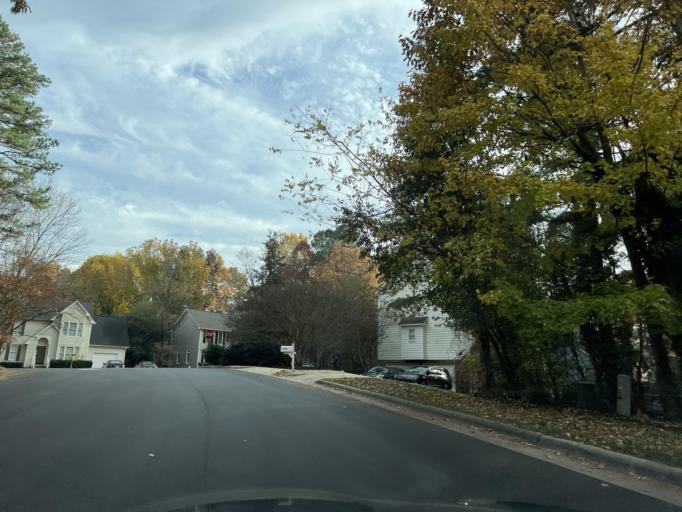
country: US
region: North Carolina
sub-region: Wake County
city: Wake Forest
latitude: 35.8992
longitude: -78.5928
